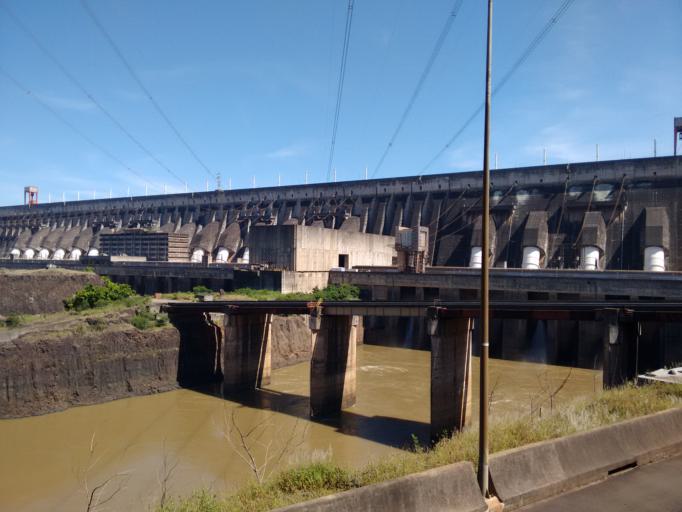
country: PY
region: Alto Parana
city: Ciudad del Este
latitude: -25.4120
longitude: -54.5857
